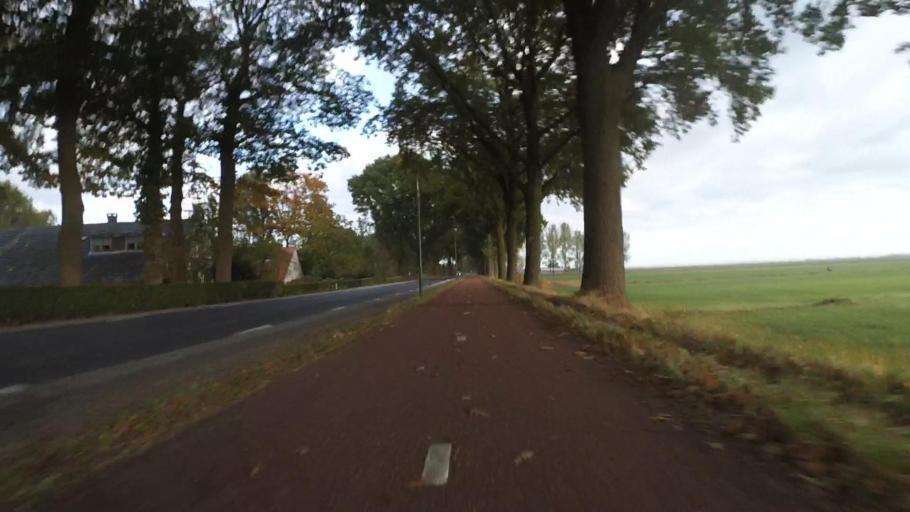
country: NL
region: Utrecht
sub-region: Gemeente Baarn
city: Baarn
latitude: 52.2351
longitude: 5.2600
